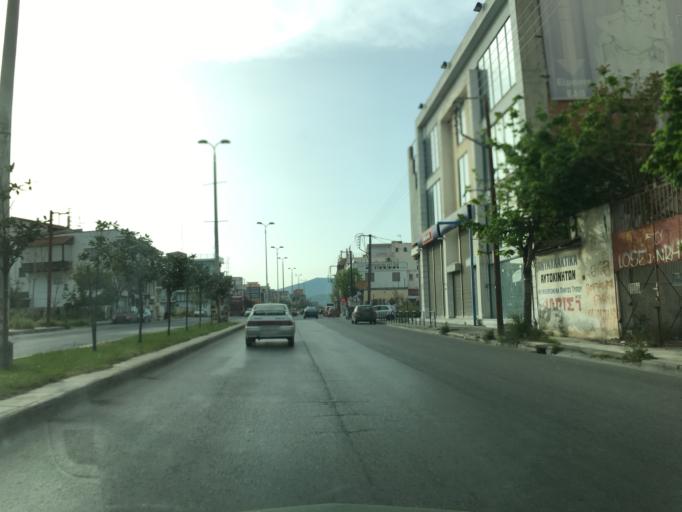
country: GR
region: Thessaly
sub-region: Nomos Magnisias
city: Nea Ionia
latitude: 39.3652
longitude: 22.9265
